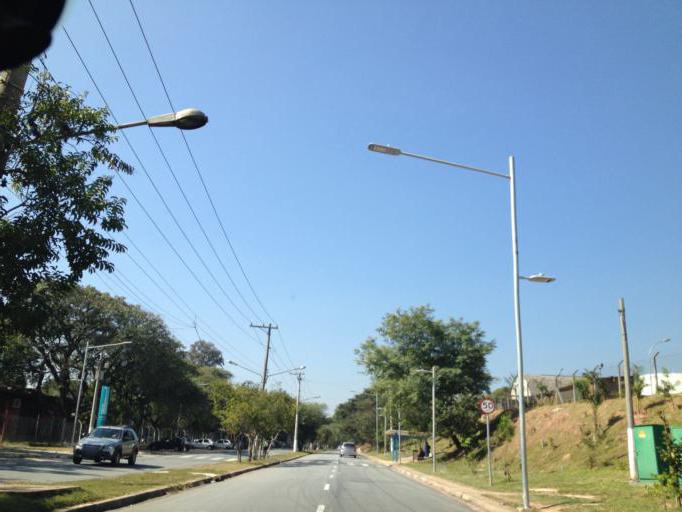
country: BR
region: Sao Paulo
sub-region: Osasco
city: Osasco
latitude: -23.5599
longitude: -46.7425
